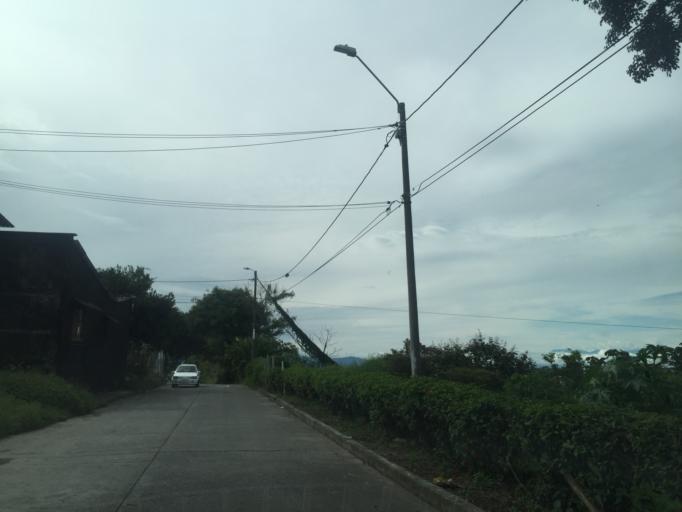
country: CO
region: Quindio
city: Armenia
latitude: 4.5237
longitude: -75.6913
